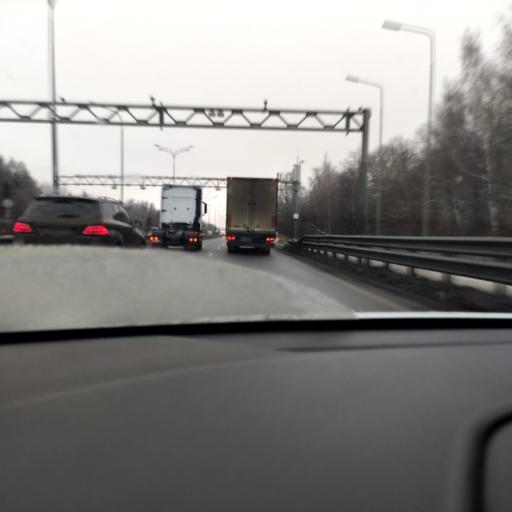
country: RU
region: Tatarstan
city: Sviyazhsk
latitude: 55.7502
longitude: 48.8000
